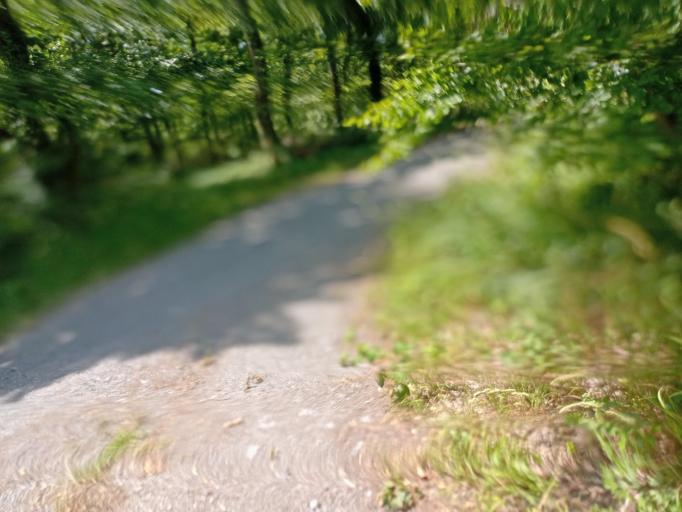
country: DE
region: Baden-Wuerttemberg
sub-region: Karlsruhe Region
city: Ubstadt-Weiher
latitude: 49.1649
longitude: 8.6505
